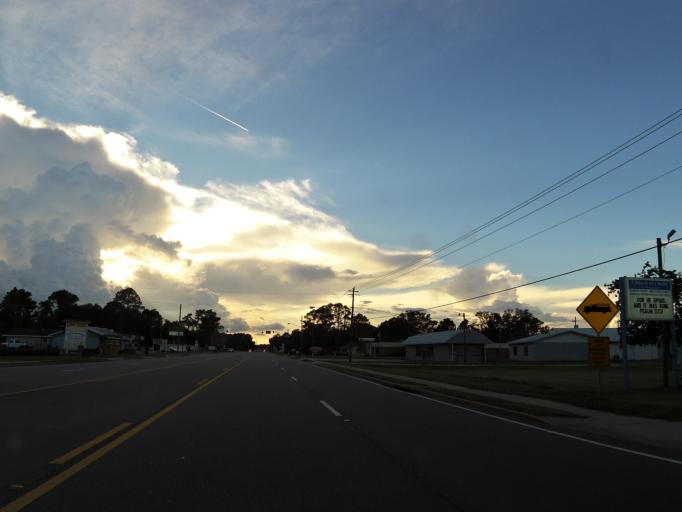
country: US
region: Georgia
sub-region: Camden County
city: St Marys
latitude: 30.7455
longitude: -81.5602
